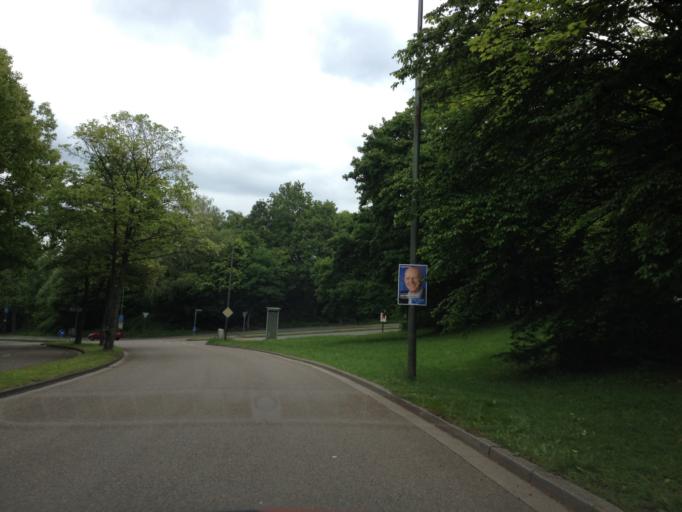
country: DE
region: North Rhine-Westphalia
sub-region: Regierungsbezirk Arnsberg
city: Bochum
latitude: 51.4502
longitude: 7.2730
